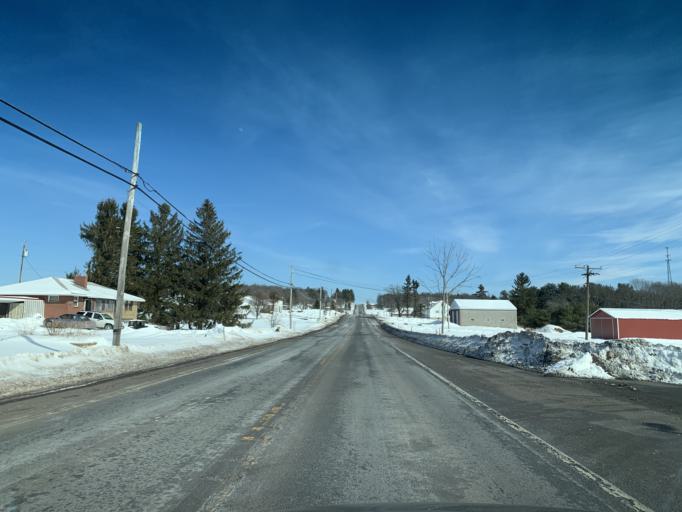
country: US
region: Maryland
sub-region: Allegany County
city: Frostburg
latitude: 39.6874
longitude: -79.0100
